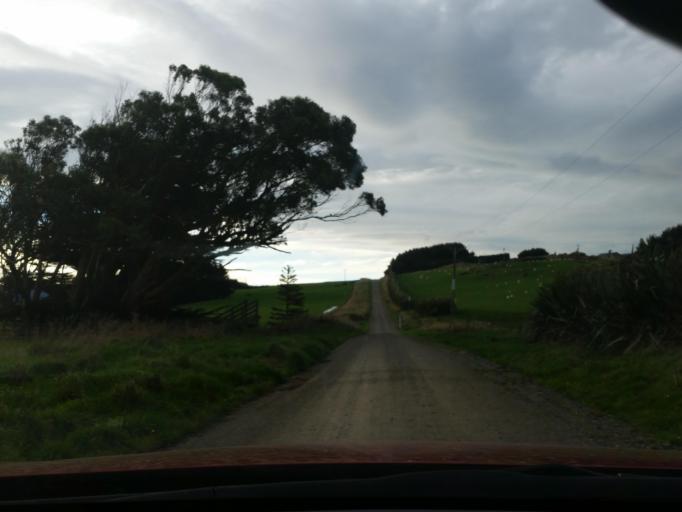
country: NZ
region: Southland
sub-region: Southland District
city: Riverton
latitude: -46.3548
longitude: 167.9245
